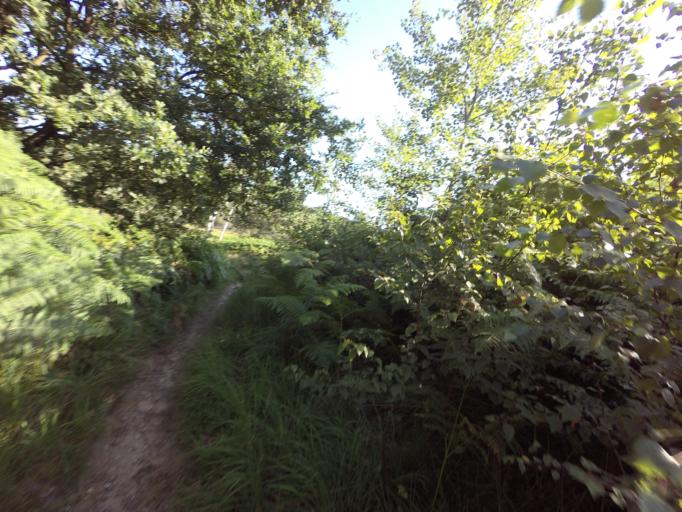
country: NL
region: Limburg
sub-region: Gemeente Roerdalen
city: Herkenbosch
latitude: 51.1784
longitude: 6.1176
